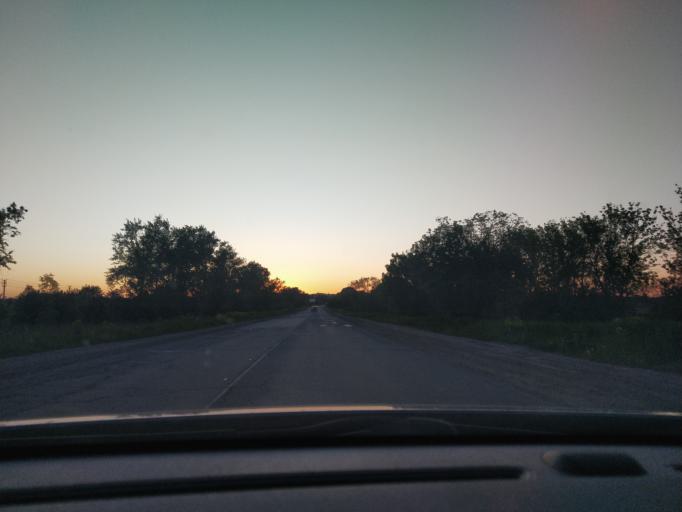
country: RU
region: St.-Petersburg
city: Krasnoye Selo
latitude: 59.7067
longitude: 30.0910
